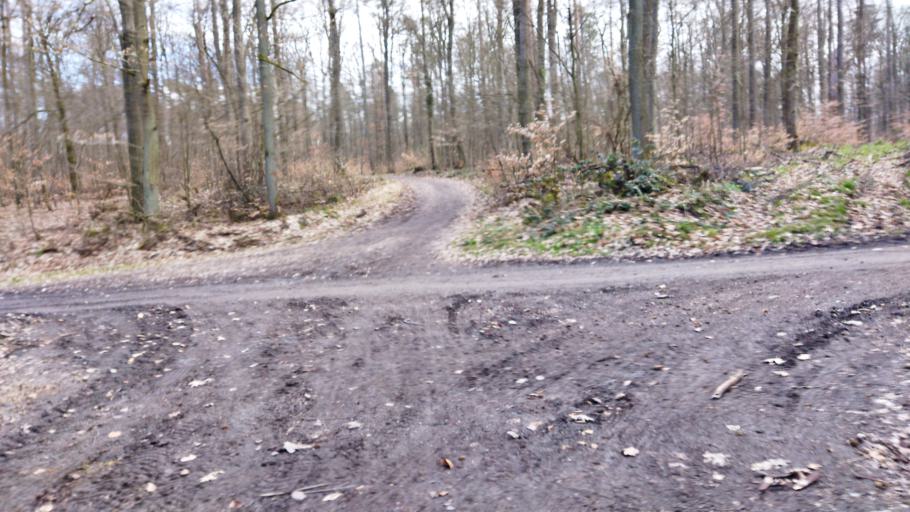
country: DE
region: Baden-Wuerttemberg
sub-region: Regierungsbezirk Stuttgart
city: Leingarten
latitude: 49.1285
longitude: 9.0869
